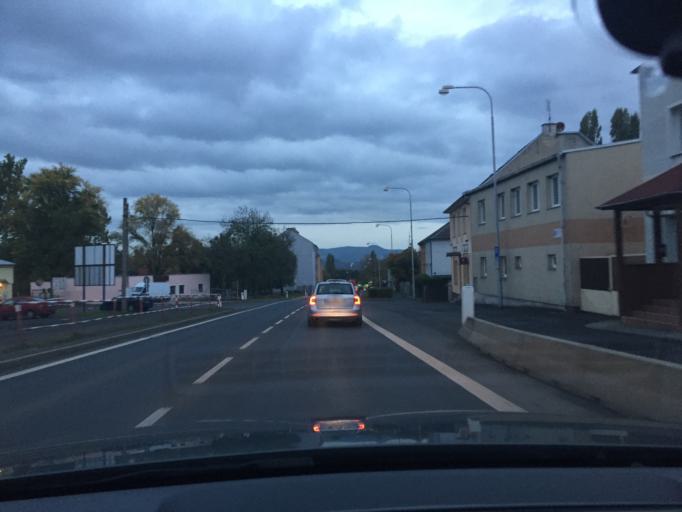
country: CZ
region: Ustecky
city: Novosedlice
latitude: 50.6577
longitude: 13.8049
